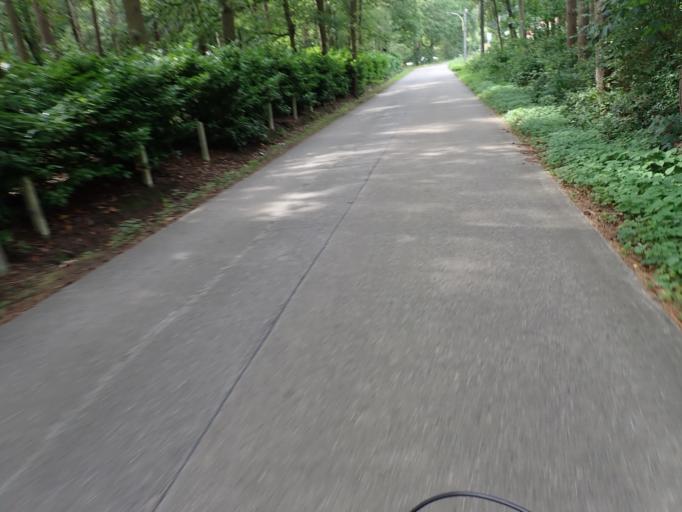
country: BE
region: Flanders
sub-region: Provincie Antwerpen
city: Zandhoven
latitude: 51.2257
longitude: 4.6411
